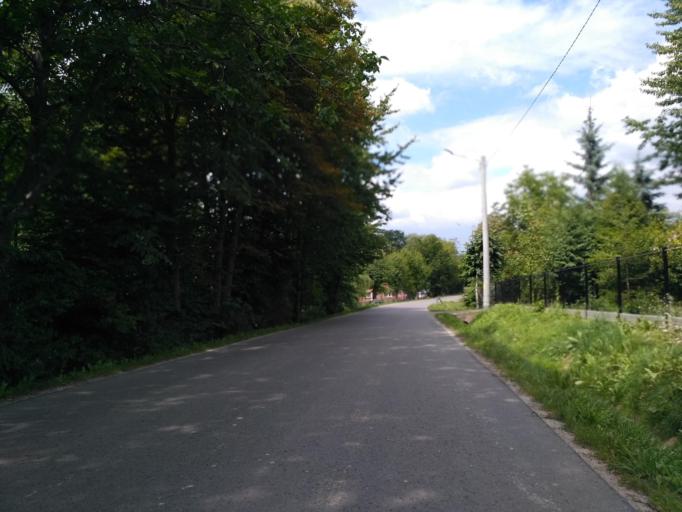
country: PL
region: Subcarpathian Voivodeship
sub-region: Powiat rzeszowski
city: Chmielnik
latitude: 49.9470
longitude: 22.1573
